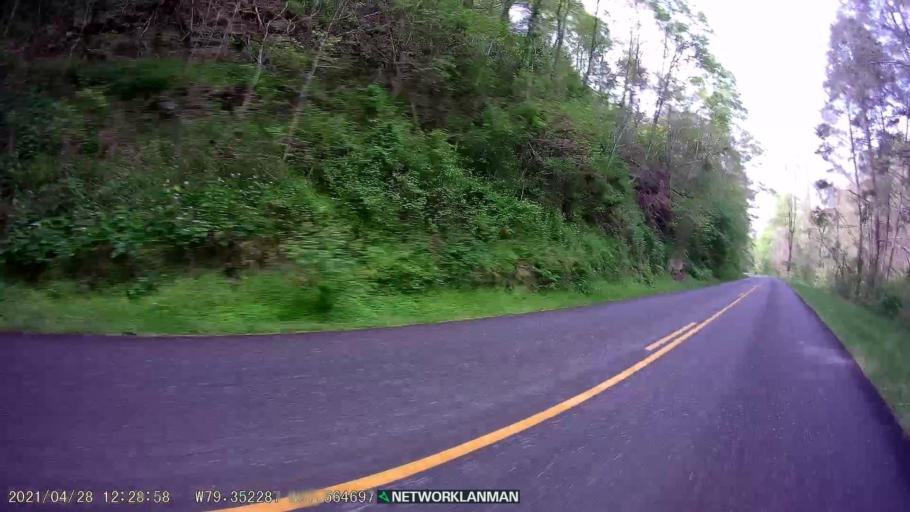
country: US
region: Virginia
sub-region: Rockbridge County
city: Glasgow
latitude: 37.5649
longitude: -79.3523
